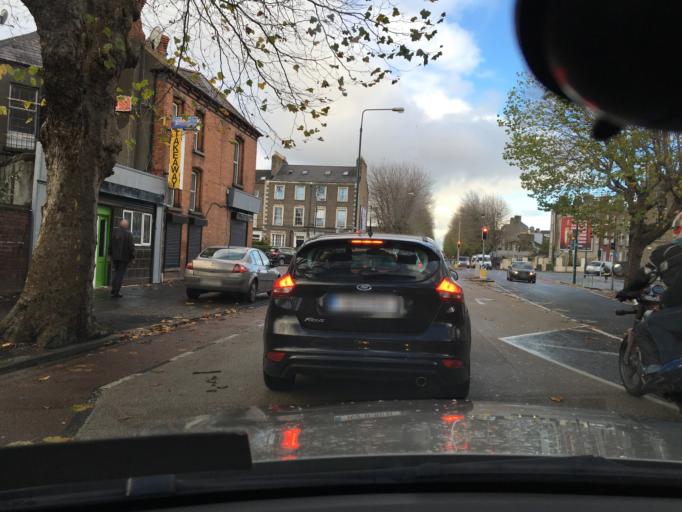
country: IE
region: Leinster
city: Drumcondra
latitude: 53.3595
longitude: -6.2597
